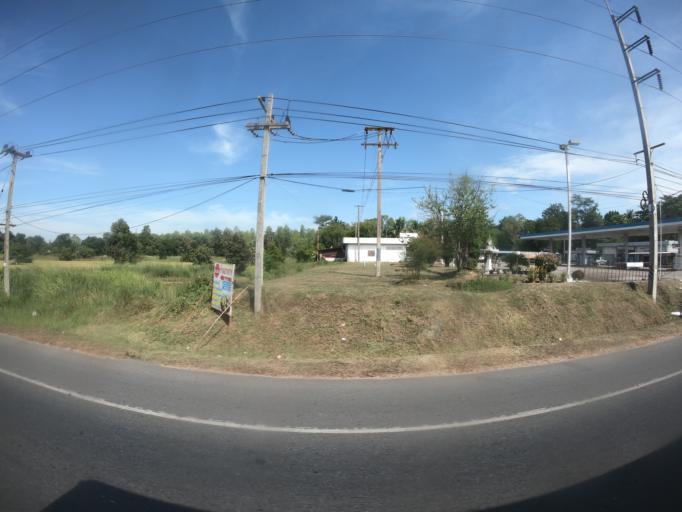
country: TH
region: Maha Sarakham
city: Chiang Yuen
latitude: 16.4418
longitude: 102.9753
